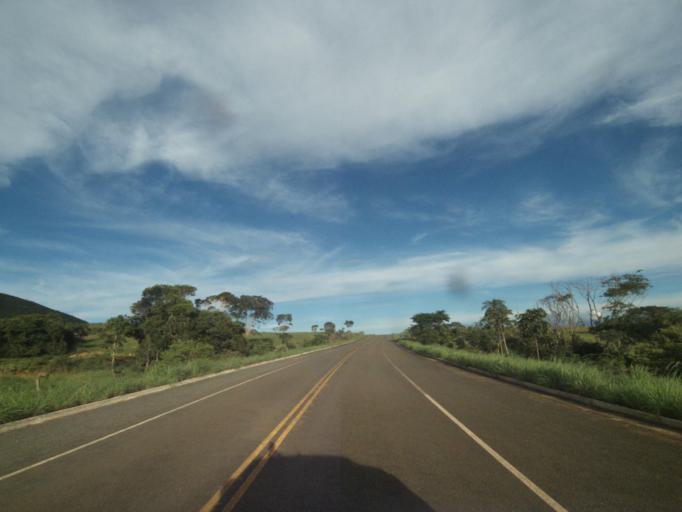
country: BR
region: Goias
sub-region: Jaragua
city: Jaragua
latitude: -15.8373
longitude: -49.3150
